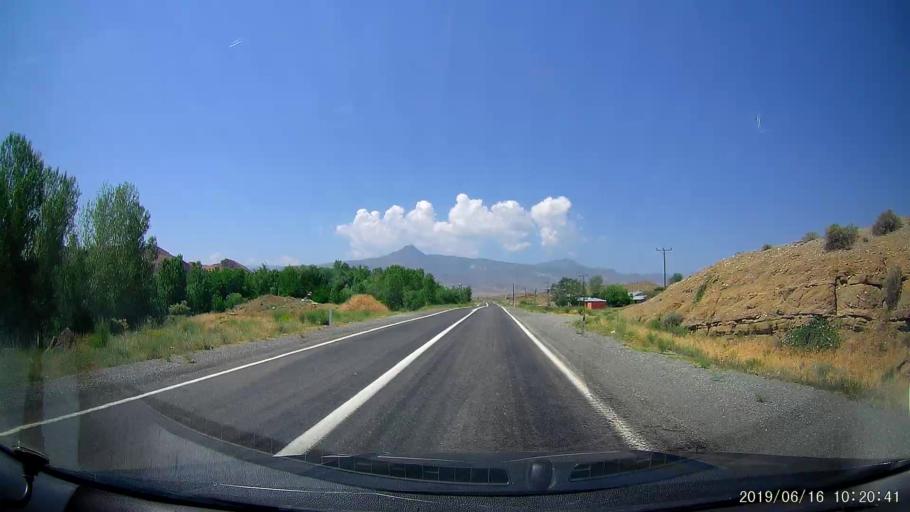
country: TR
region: Igdir
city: Tuzluca
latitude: 40.1455
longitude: 43.6451
